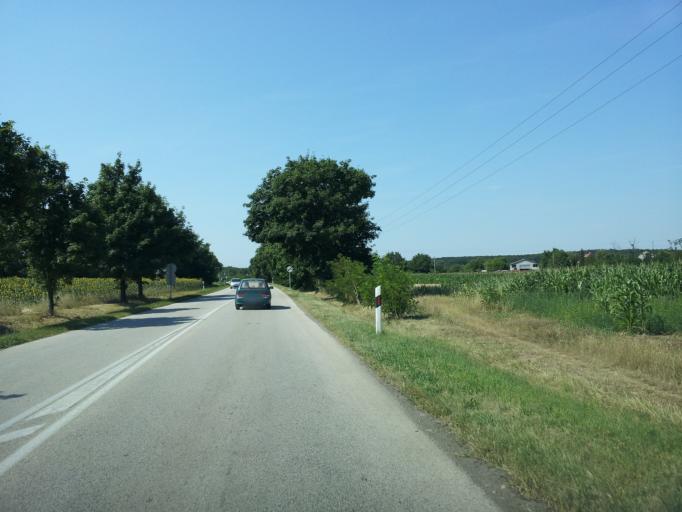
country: HU
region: Fejer
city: Pakozd
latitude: 47.2569
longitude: 18.5164
